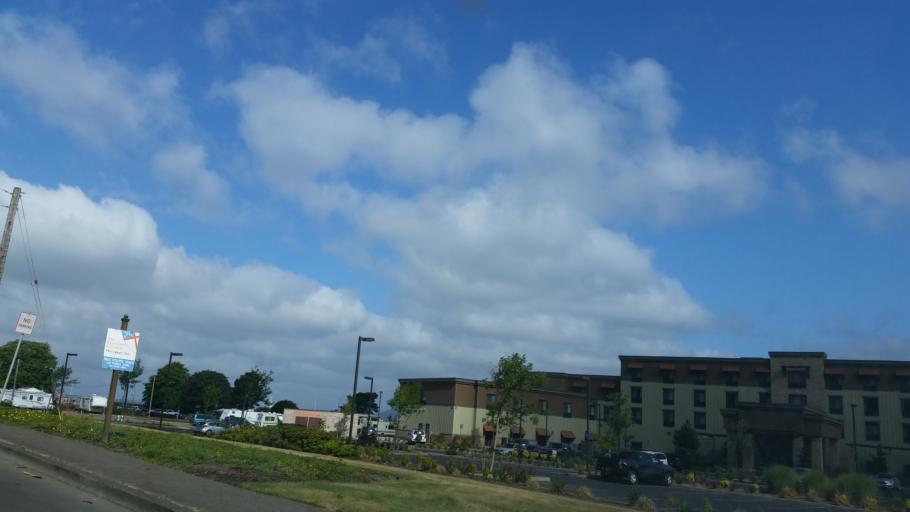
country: US
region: Oregon
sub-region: Clatsop County
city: Astoria
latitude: 46.1938
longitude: -123.7988
